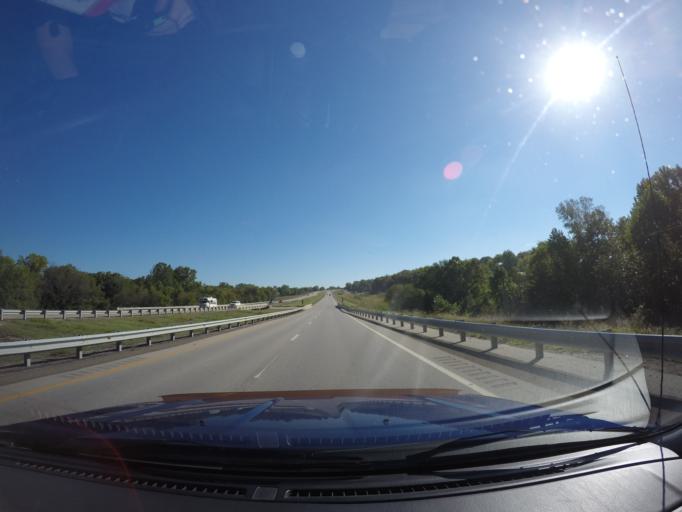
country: US
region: Kansas
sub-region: Pottawatomie County
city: Wamego
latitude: 39.2056
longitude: -96.4248
